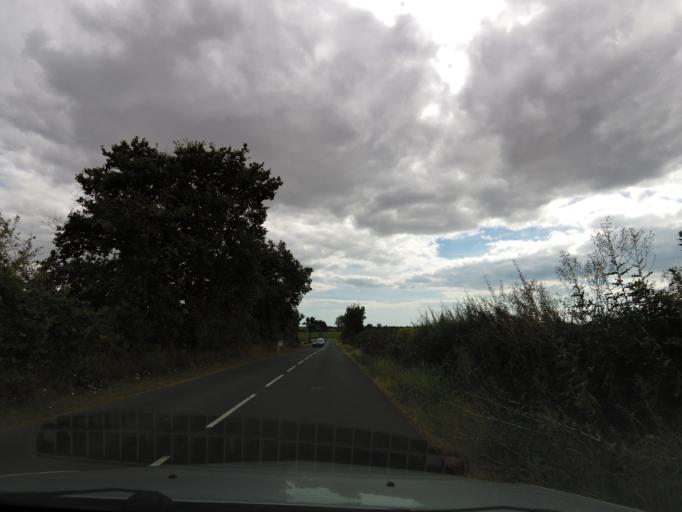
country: FR
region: Pays de la Loire
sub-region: Departement de la Vendee
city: Avrille
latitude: 46.4571
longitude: -1.4587
